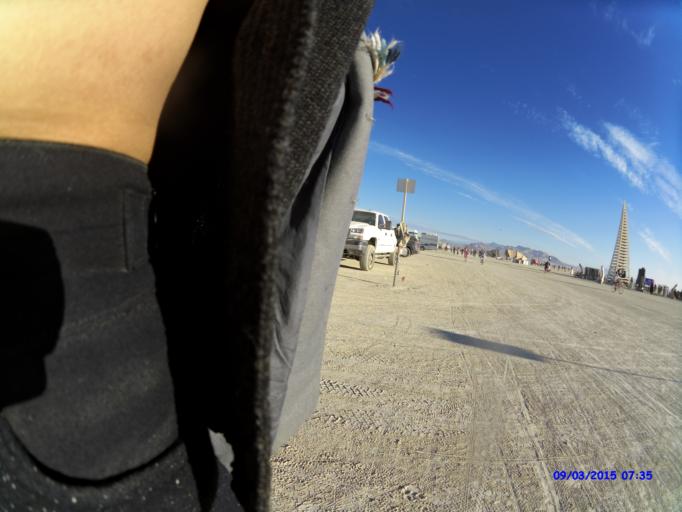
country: US
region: Nevada
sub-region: Pershing County
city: Lovelock
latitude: 40.7942
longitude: -119.2094
